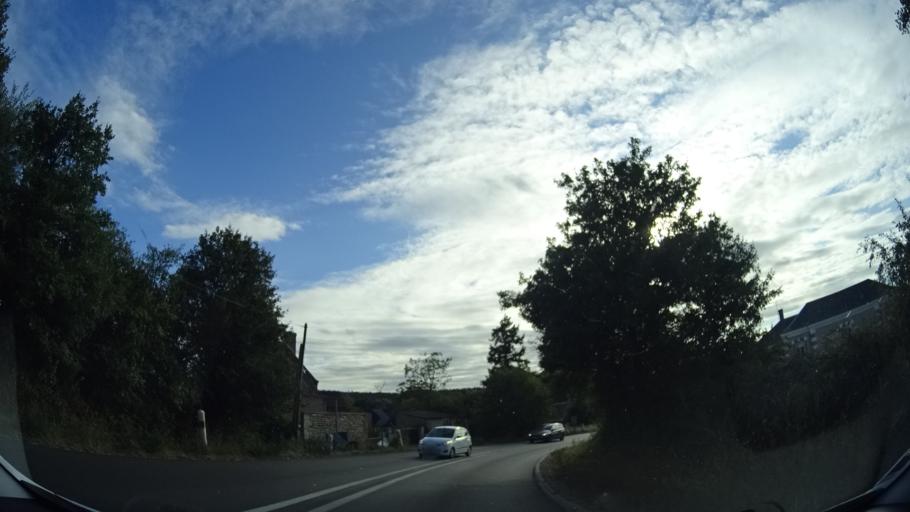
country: FR
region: Centre
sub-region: Departement du Loir-et-Cher
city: La Ville-aux-Clercs
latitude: 47.8925
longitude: 1.1330
